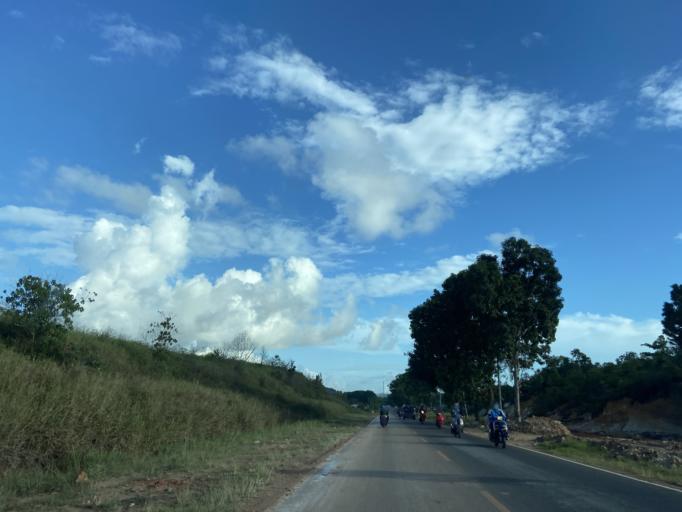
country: SG
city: Singapore
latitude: 1.0206
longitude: 104.0134
